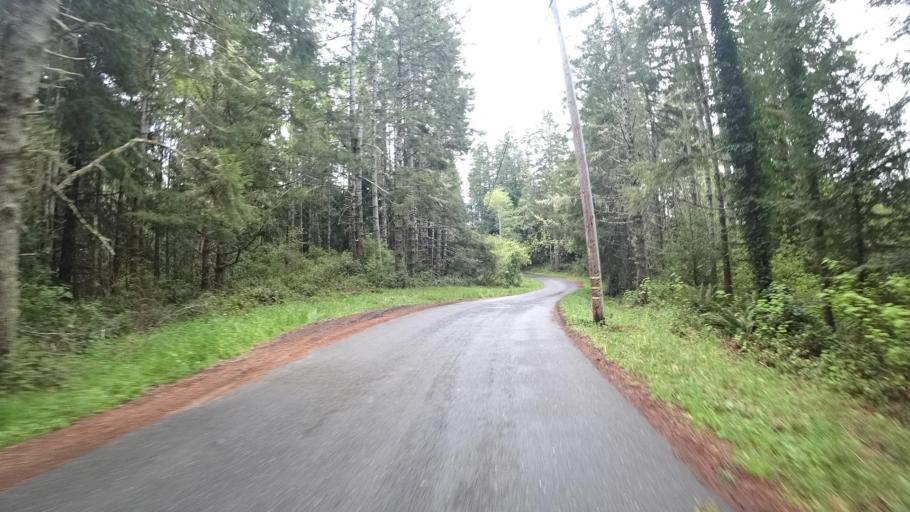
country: US
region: California
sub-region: Humboldt County
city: Bayside
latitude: 40.8272
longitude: -124.0099
